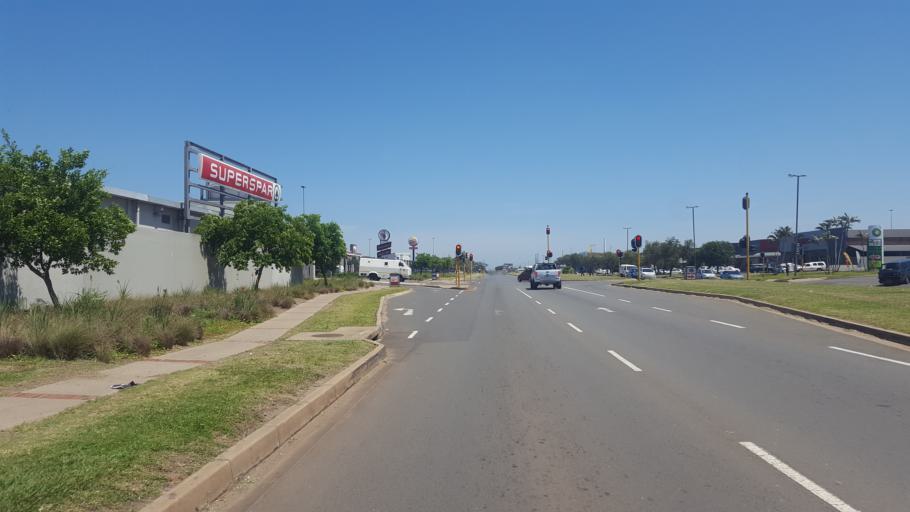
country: ZA
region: KwaZulu-Natal
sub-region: uThungulu District Municipality
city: Richards Bay
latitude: -28.7462
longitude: 32.0504
